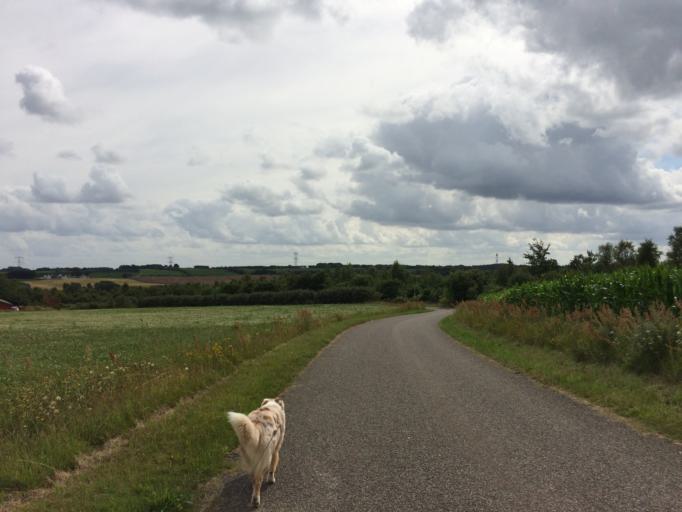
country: DK
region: Central Jutland
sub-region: Viborg Kommune
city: Viborg
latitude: 56.4959
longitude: 9.5310
